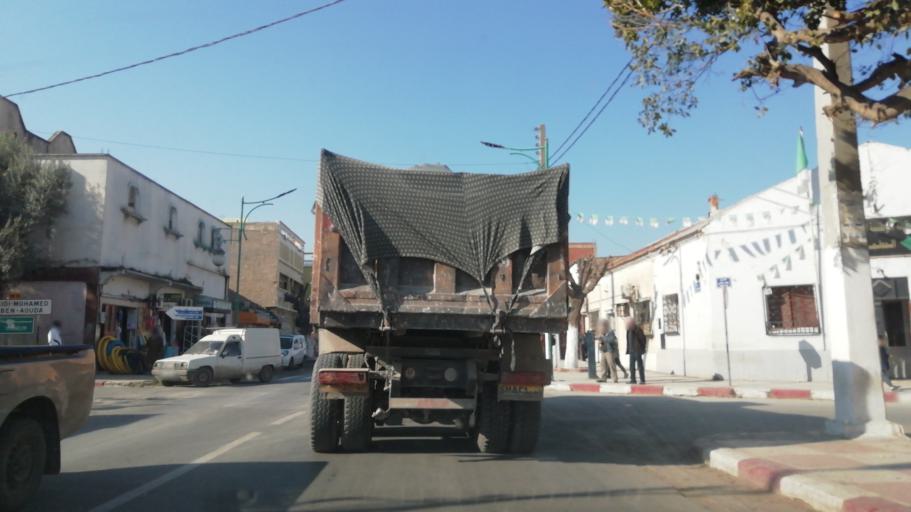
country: DZ
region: Relizane
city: Relizane
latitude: 35.7339
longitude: 0.4622
